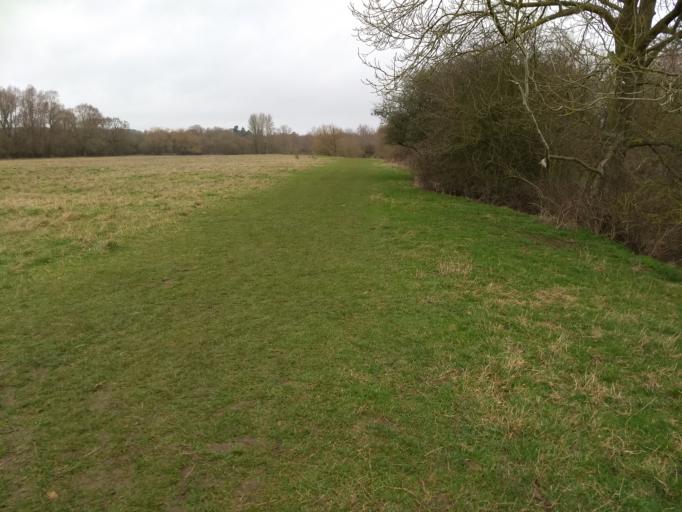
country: GB
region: England
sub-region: Bedford
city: Odell
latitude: 52.2027
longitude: -0.5907
